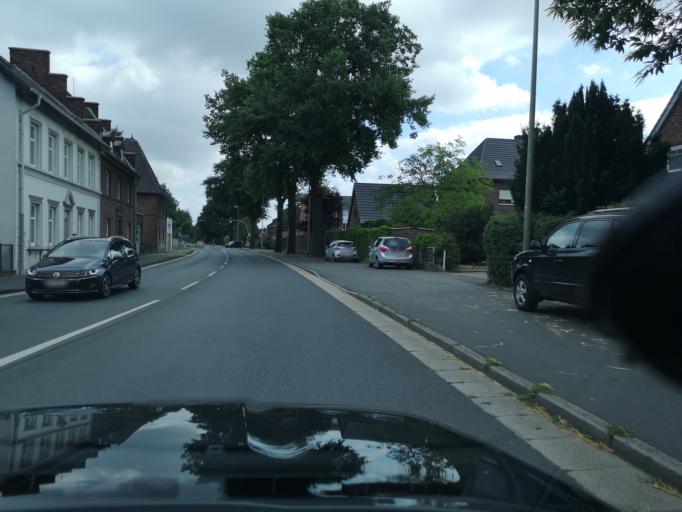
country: DE
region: North Rhine-Westphalia
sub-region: Regierungsbezirk Dusseldorf
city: Wesel
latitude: 51.6717
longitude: 6.6390
